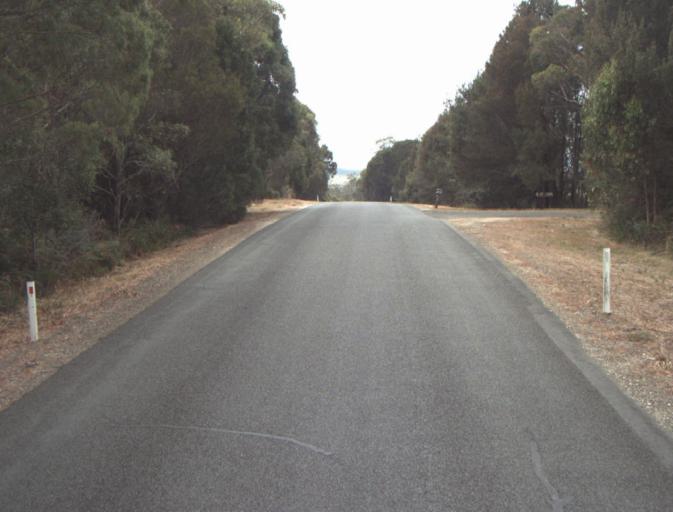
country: AU
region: Tasmania
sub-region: Launceston
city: Mayfield
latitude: -41.2198
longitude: 147.0489
